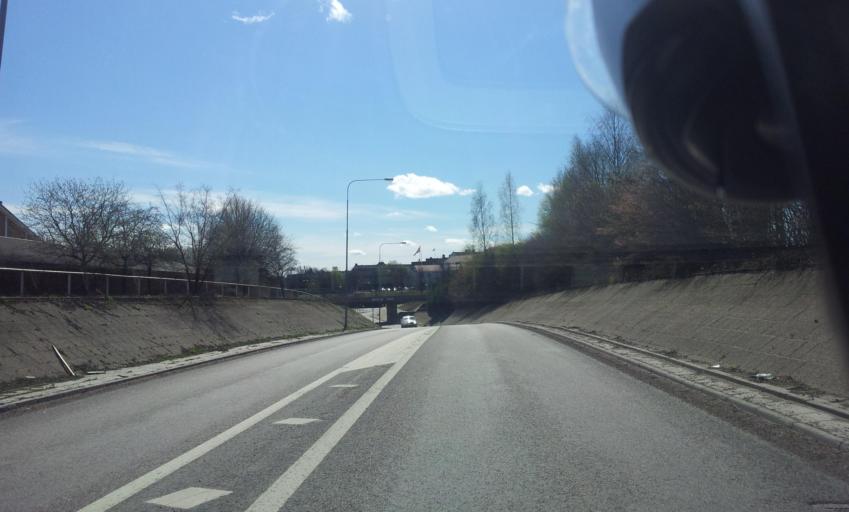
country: SE
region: Dalarna
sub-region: Borlange Kommun
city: Borlaenge
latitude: 60.4917
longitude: 15.4334
